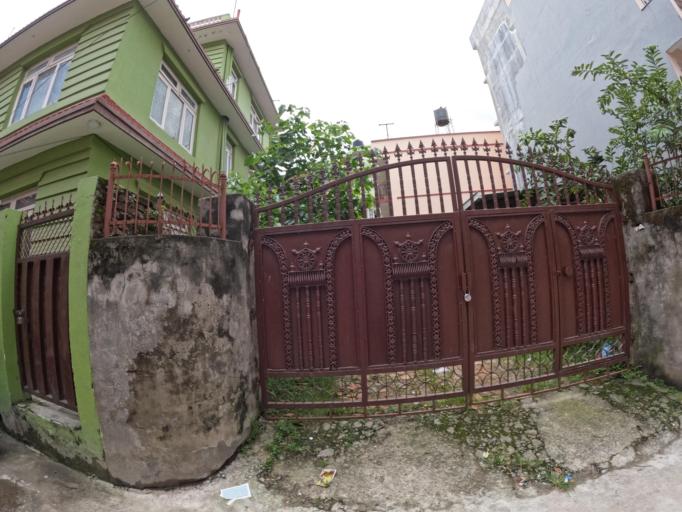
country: NP
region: Central Region
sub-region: Bagmati Zone
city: Kathmandu
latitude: 27.7397
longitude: 85.3126
